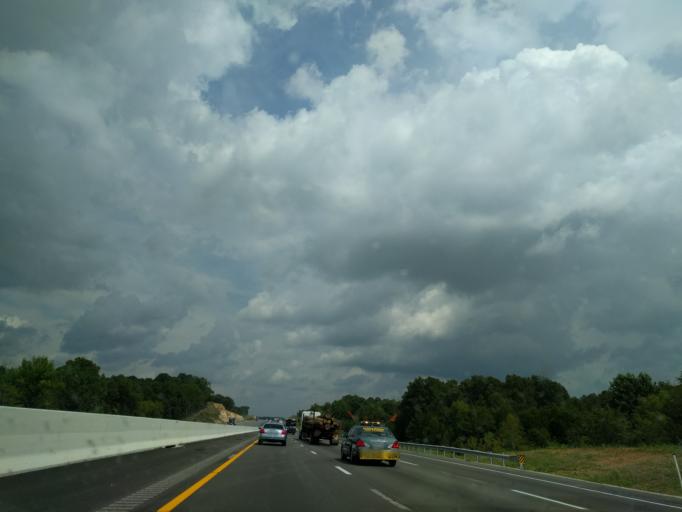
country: US
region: Kentucky
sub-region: Hart County
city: Munfordville
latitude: 37.4140
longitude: -85.8817
